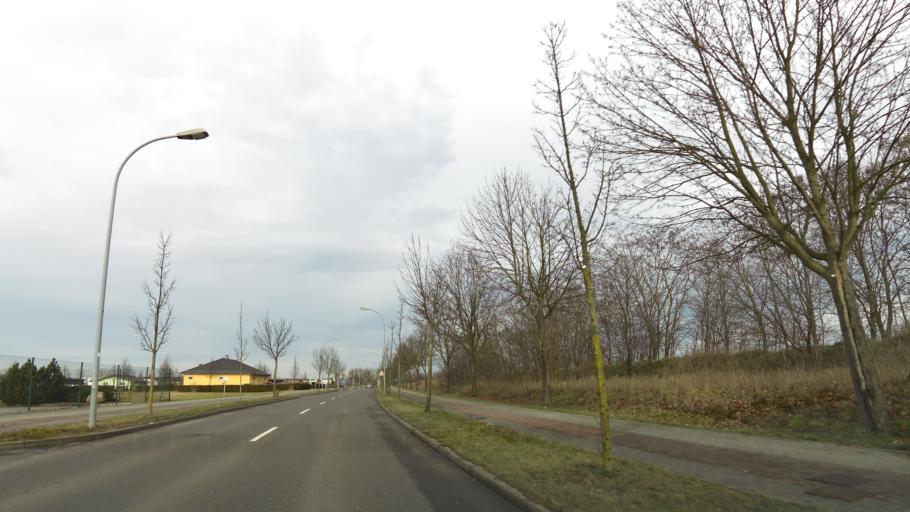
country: DE
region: Brandenburg
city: Strausberg
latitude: 52.5840
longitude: 13.9087
